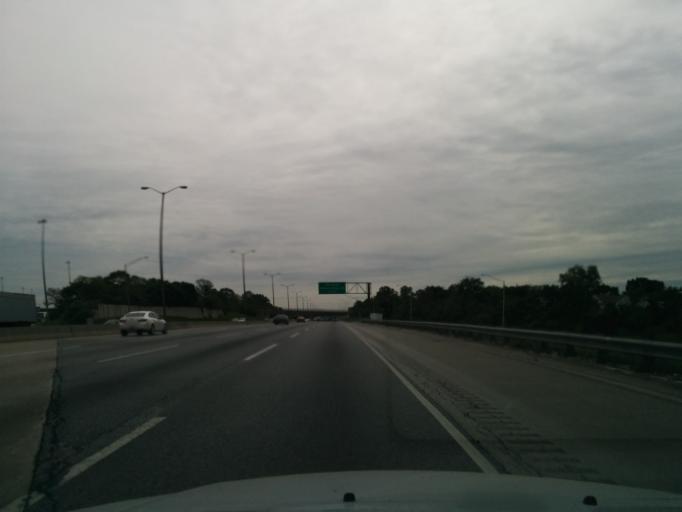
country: US
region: Illinois
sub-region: Cook County
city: Indian Head Park
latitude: 41.7607
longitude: -87.8927
